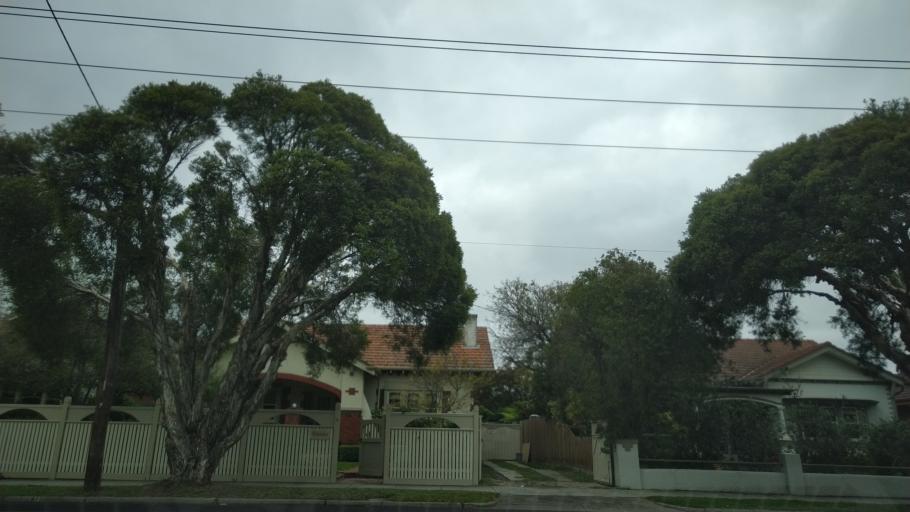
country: AU
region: Victoria
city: Murrumbeena
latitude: -37.8977
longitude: 145.0740
